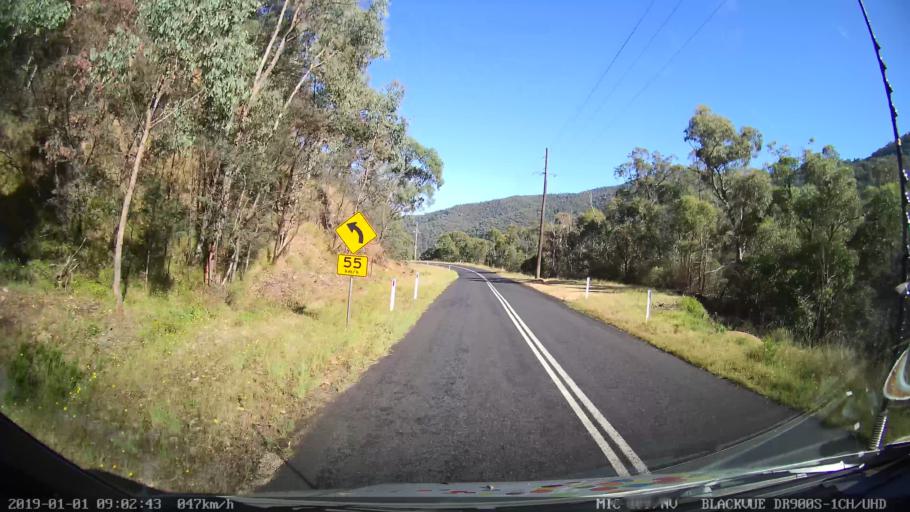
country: AU
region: New South Wales
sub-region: Snowy River
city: Jindabyne
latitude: -36.2269
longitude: 148.1698
